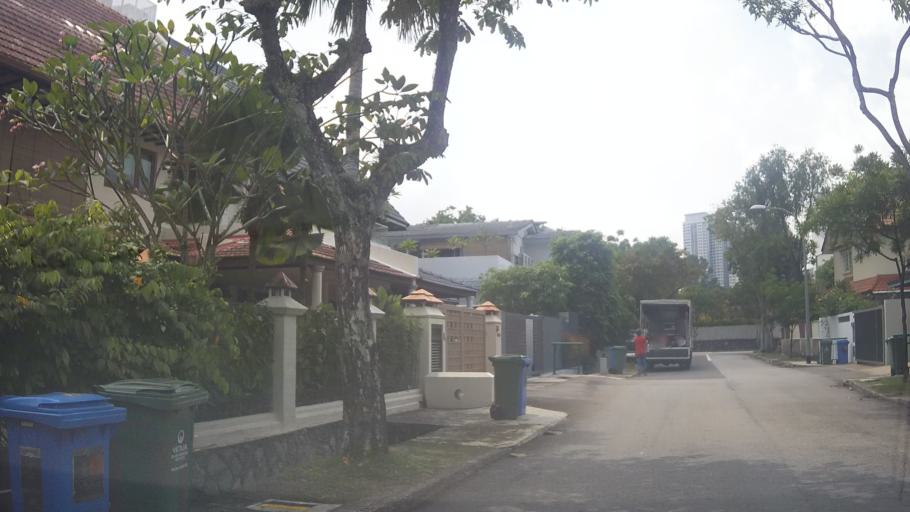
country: SG
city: Singapore
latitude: 1.3162
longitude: 103.7873
